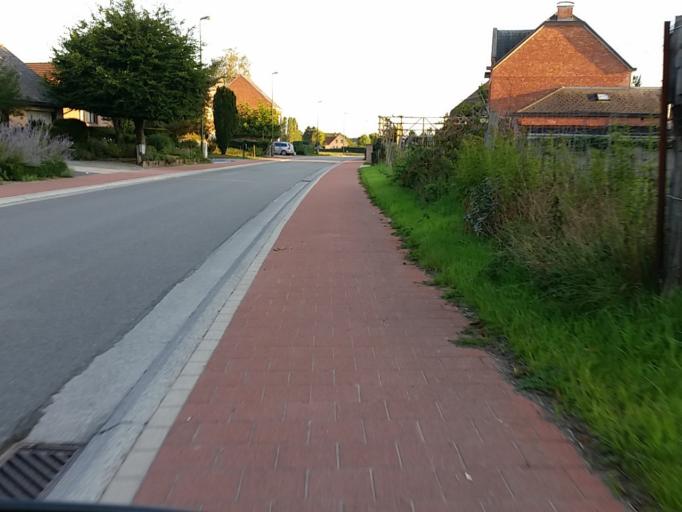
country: BE
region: Flanders
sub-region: Provincie Vlaams-Brabant
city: Kampenhout
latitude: 50.9517
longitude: 4.5627
